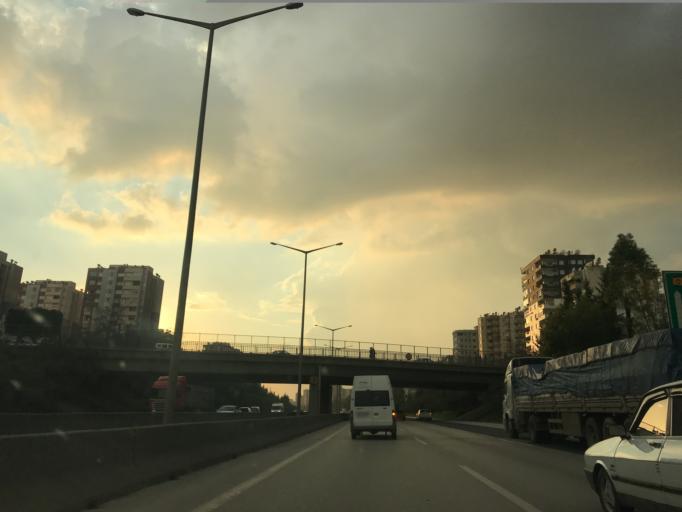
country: TR
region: Adana
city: Adana
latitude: 37.0328
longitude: 35.3012
